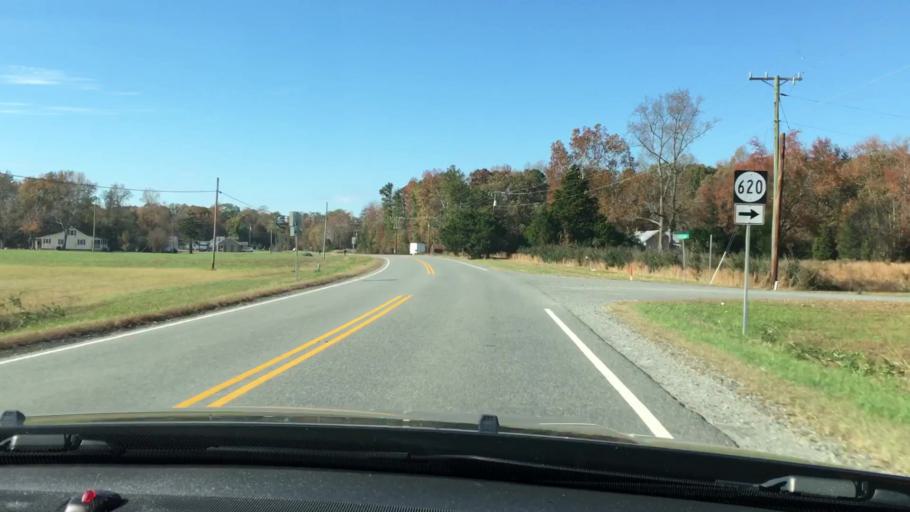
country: US
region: Virginia
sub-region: King William County
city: King William
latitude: 37.6721
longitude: -76.9740
